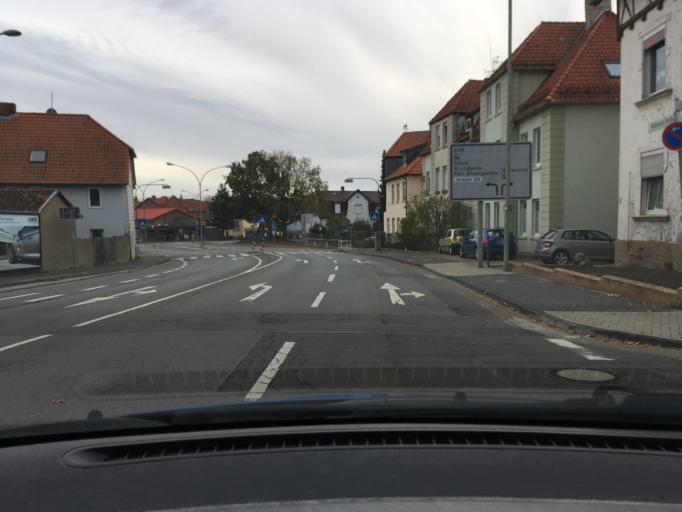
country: DE
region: Lower Saxony
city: Helmstedt
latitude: 52.2346
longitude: 11.0079
